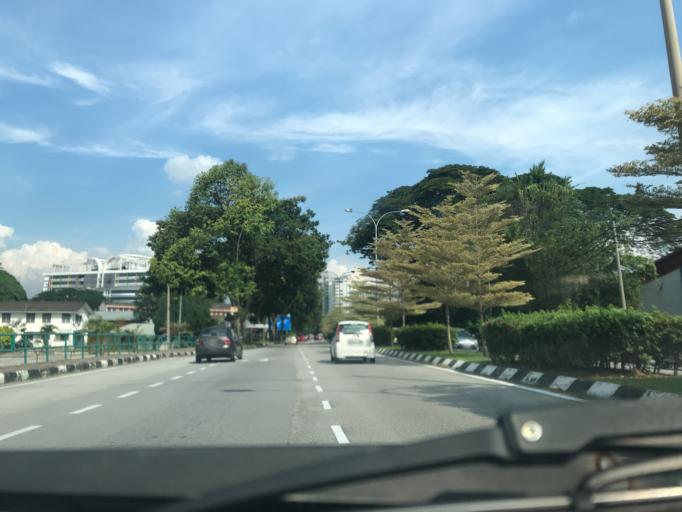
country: MY
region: Perak
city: Ipoh
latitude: 4.6066
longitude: 101.0851
